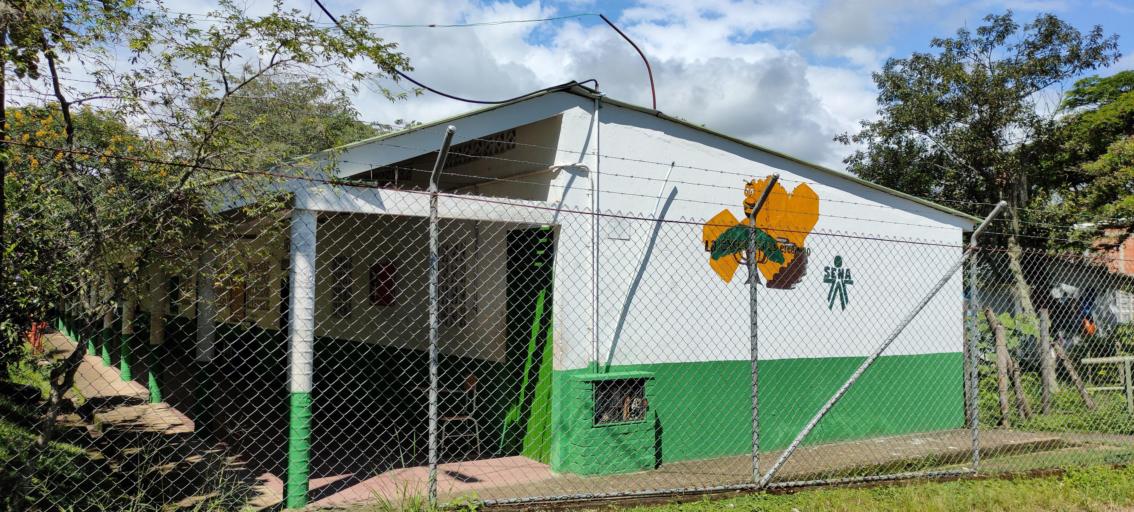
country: CO
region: Cauca
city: Buenos Aires
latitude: 3.1269
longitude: -76.5936
